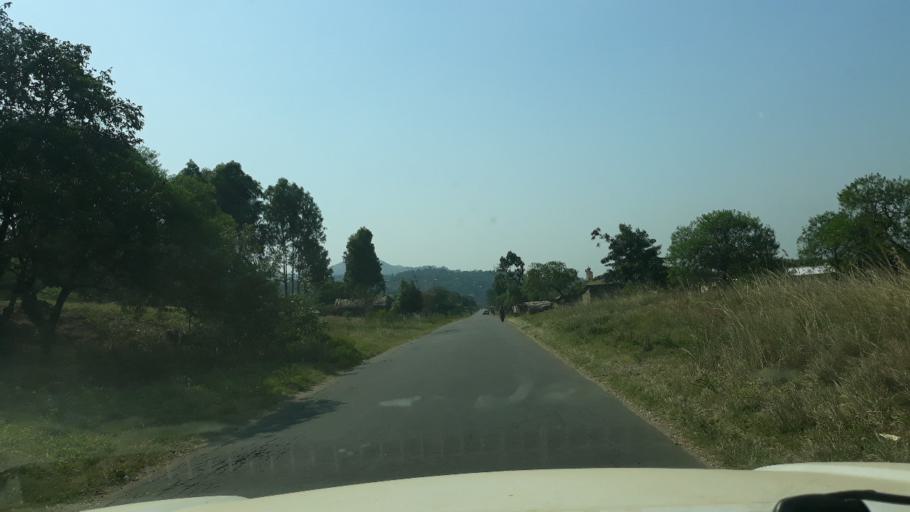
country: CD
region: South Kivu
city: Uvira
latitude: -3.2497
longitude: 29.1612
